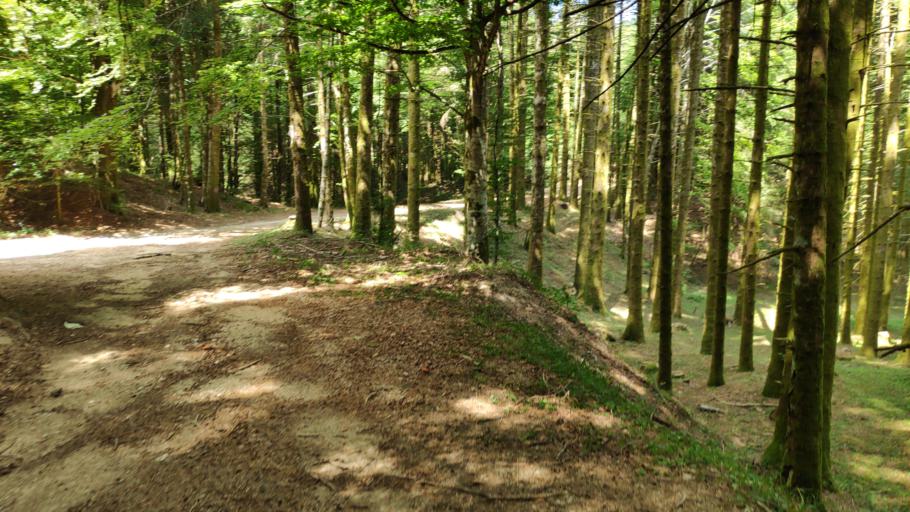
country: IT
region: Calabria
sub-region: Provincia di Vibo-Valentia
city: Serra San Bruno
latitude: 38.5416
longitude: 16.3610
